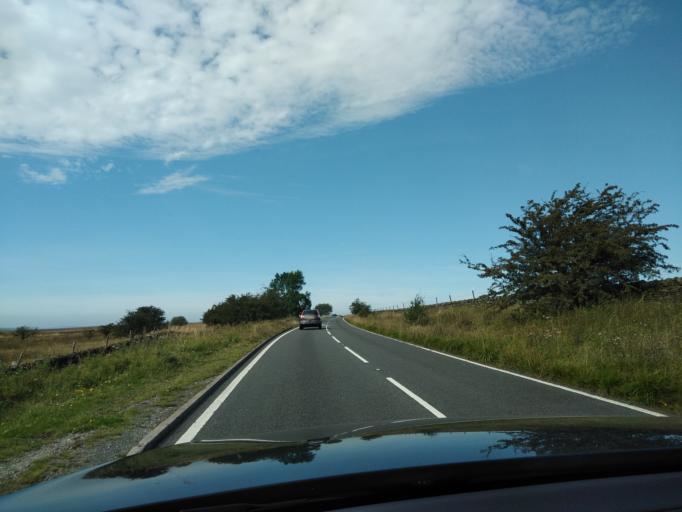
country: GB
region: England
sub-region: Derbyshire
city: Hathersage
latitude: 53.2962
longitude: -1.5736
